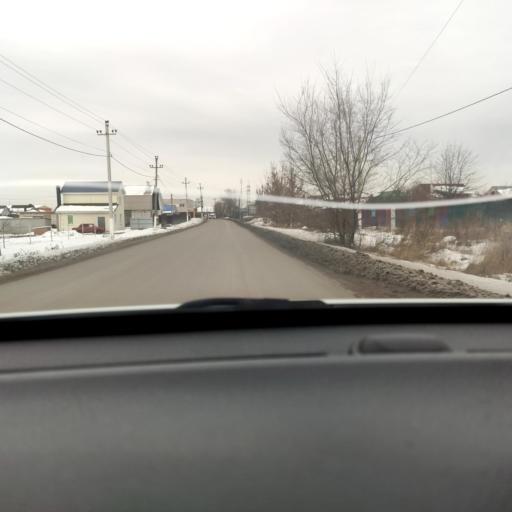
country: RU
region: Voronezj
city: Somovo
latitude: 51.6731
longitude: 39.3374
